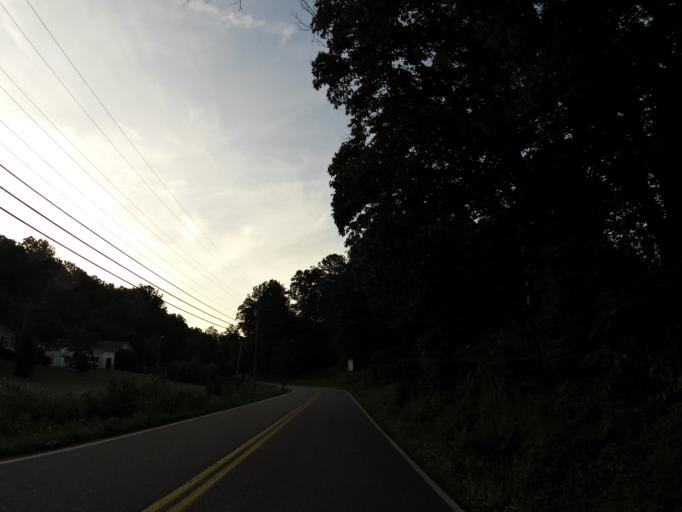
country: US
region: Tennessee
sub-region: Blount County
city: Maryville
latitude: 35.6617
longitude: -83.9619
